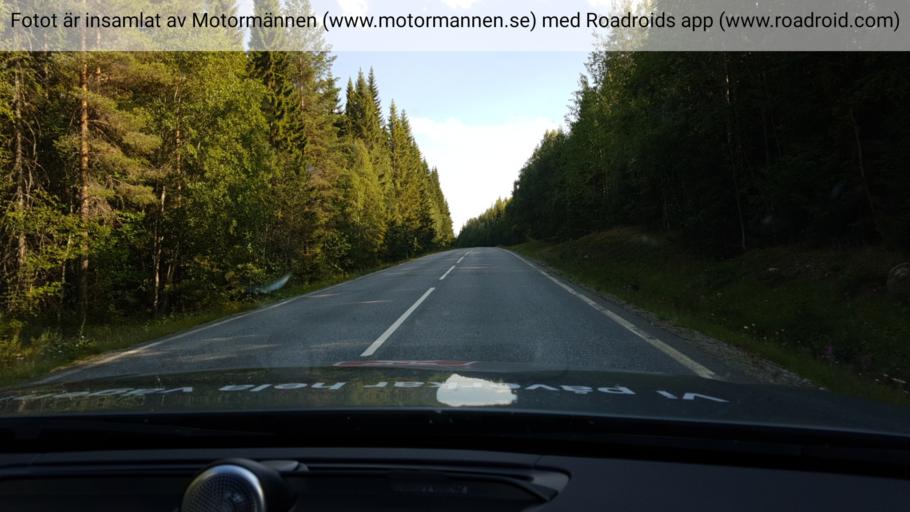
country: SE
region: Vaesterbotten
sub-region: Dorotea Kommun
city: Dorotea
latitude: 63.8750
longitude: 16.3748
